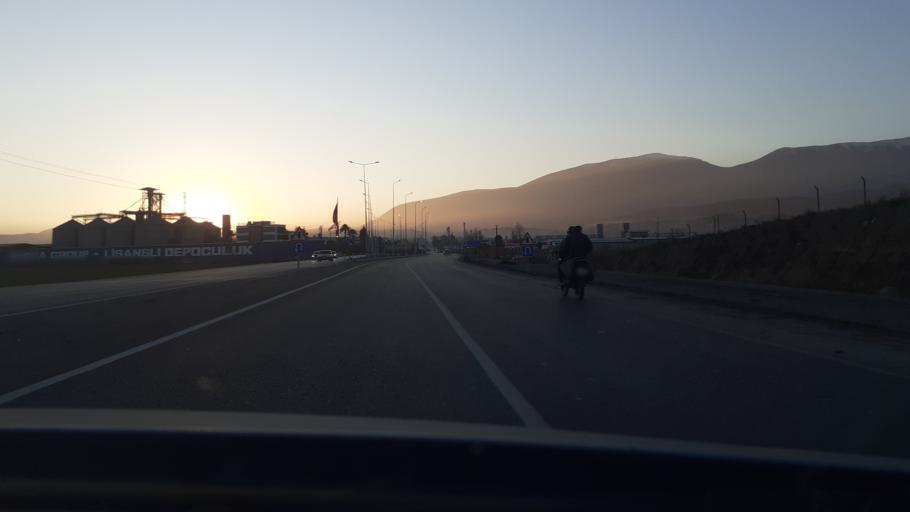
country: TR
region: Hatay
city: Kirikhan
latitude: 36.5023
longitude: 36.3922
